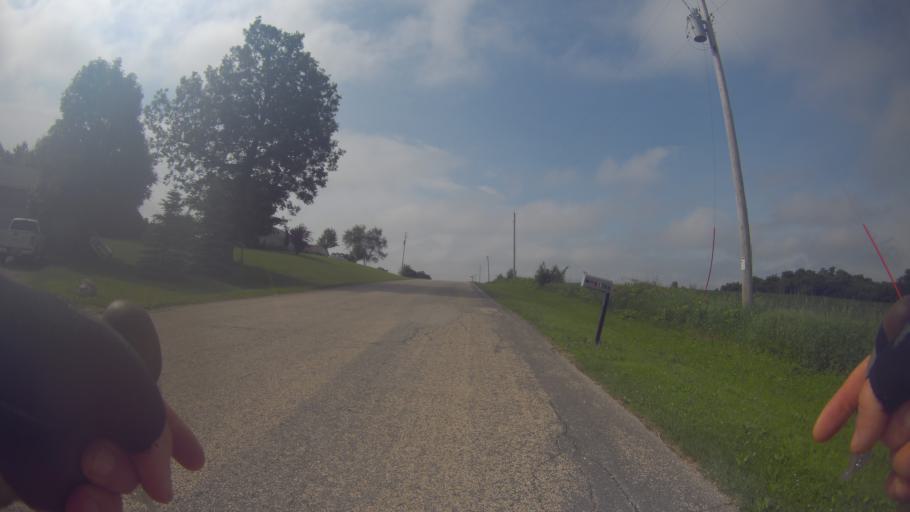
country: US
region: Wisconsin
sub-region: Dane County
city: Stoughton
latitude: 42.9433
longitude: -89.1811
